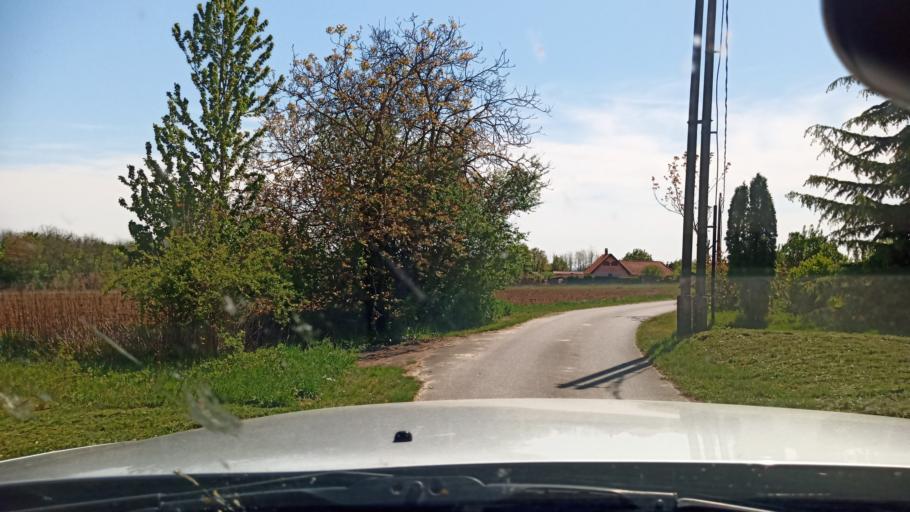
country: HU
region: Zala
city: Heviz
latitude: 46.7644
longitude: 17.1473
